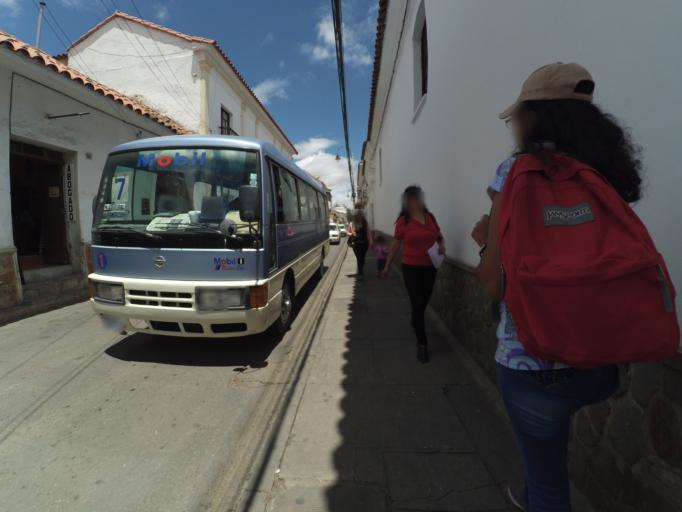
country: BO
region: Chuquisaca
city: Sucre
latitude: -19.0447
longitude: -65.2608
